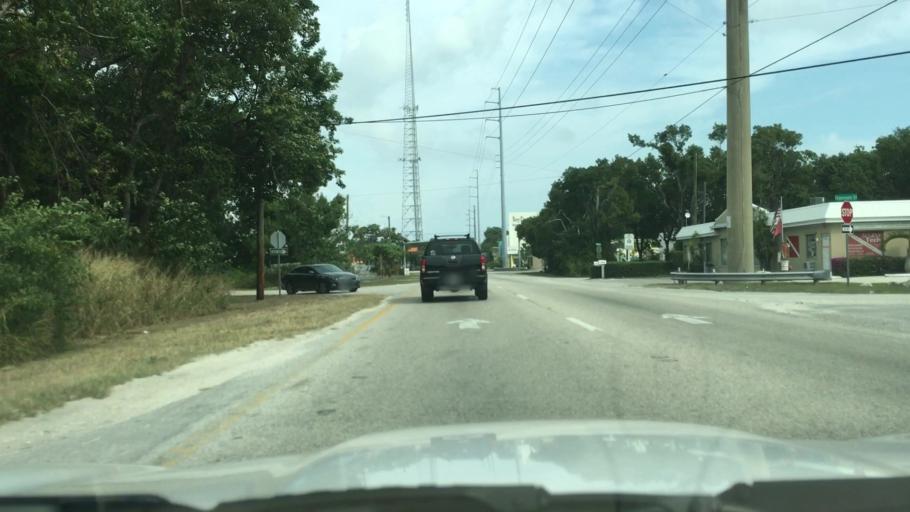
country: US
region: Florida
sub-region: Monroe County
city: Key Largo
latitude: 25.0890
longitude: -80.4459
